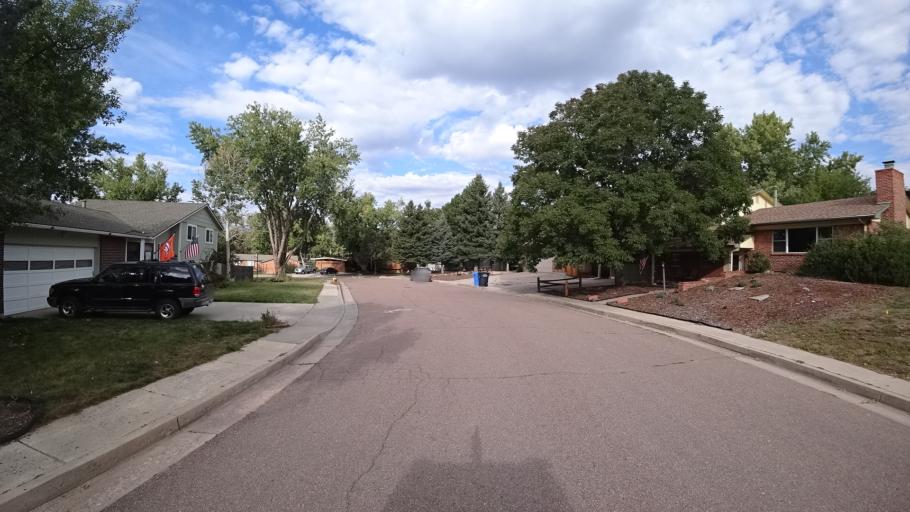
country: US
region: Colorado
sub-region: El Paso County
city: Cimarron Hills
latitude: 38.8633
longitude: -104.7504
